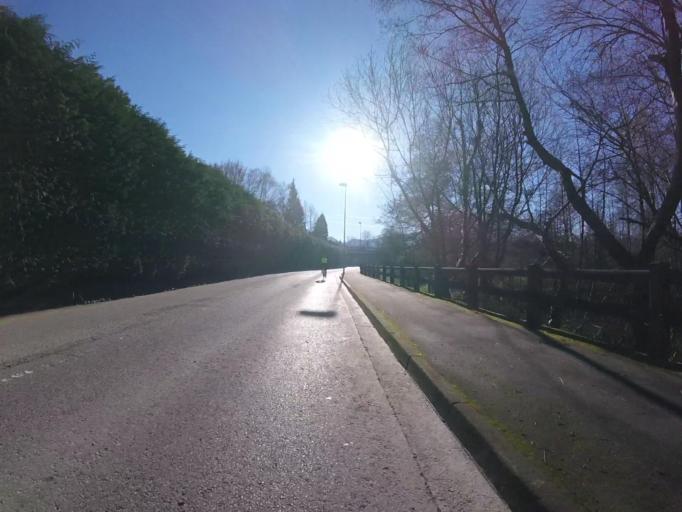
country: ES
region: Basque Country
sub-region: Provincia de Guipuzcoa
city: Irun
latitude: 43.3352
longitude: -1.7776
